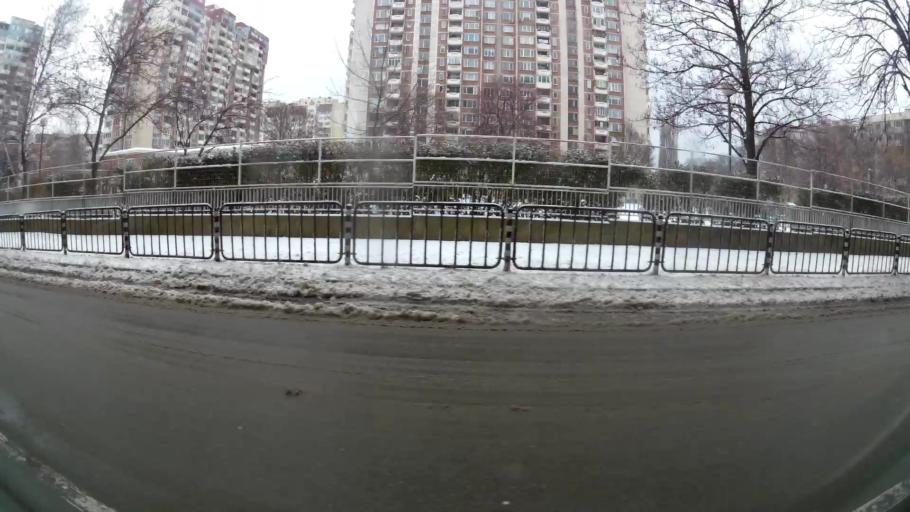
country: BG
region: Sofia-Capital
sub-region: Stolichna Obshtina
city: Sofia
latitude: 42.6974
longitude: 23.3035
